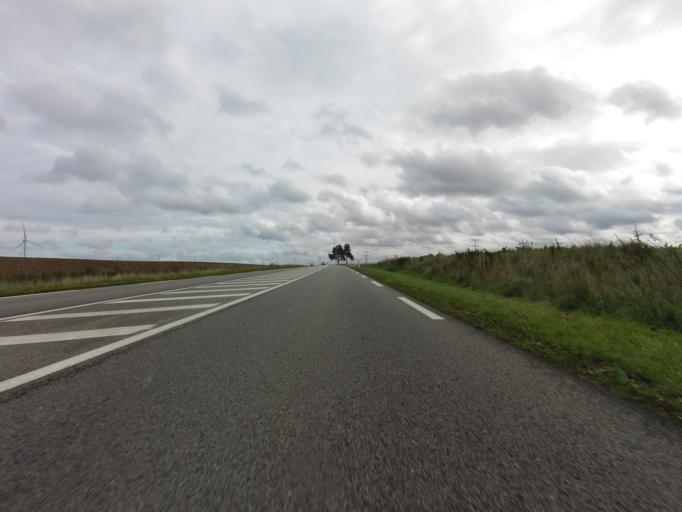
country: FR
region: Haute-Normandie
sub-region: Departement de la Seine-Maritime
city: Criel-sur-Mer
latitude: 50.0186
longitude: 1.3568
